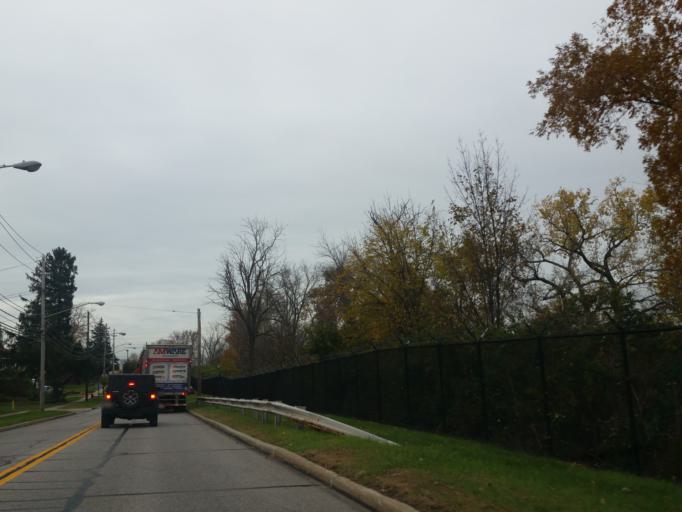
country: US
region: Ohio
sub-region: Cuyahoga County
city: Newburgh Heights
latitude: 41.4242
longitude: -81.6564
